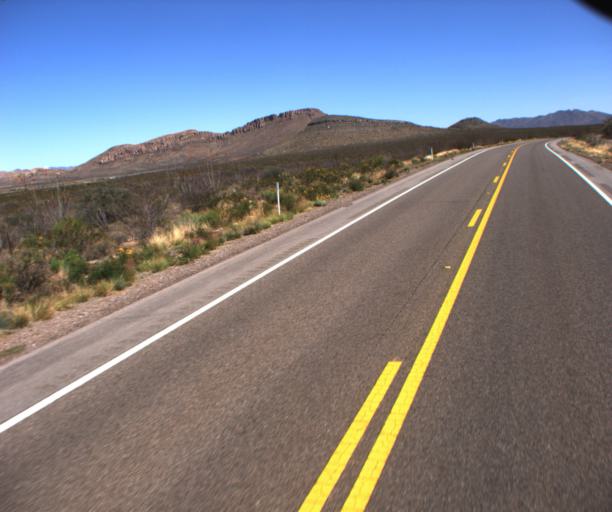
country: US
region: Arizona
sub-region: Cochise County
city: Douglas
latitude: 31.4404
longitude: -109.4768
